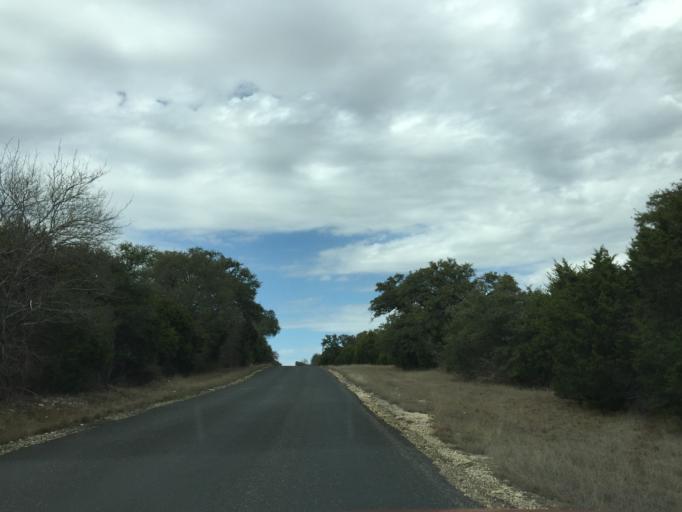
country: US
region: Texas
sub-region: Burnet County
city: Bertram
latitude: 30.7408
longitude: -97.9377
